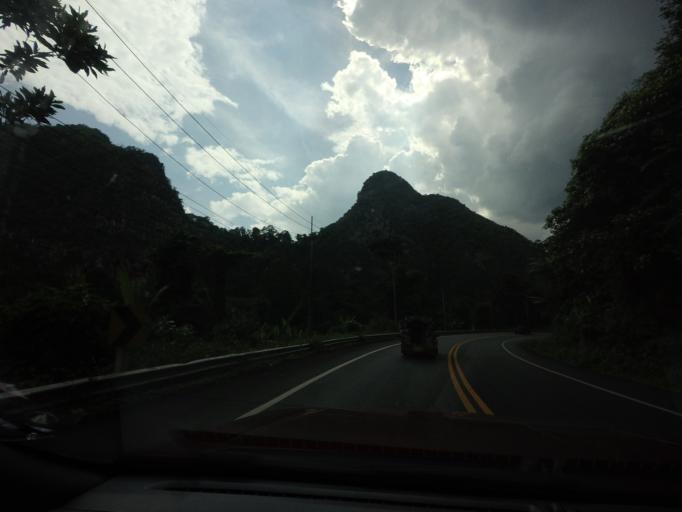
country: TH
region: Yala
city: Than To
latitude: 6.2097
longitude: 101.1676
